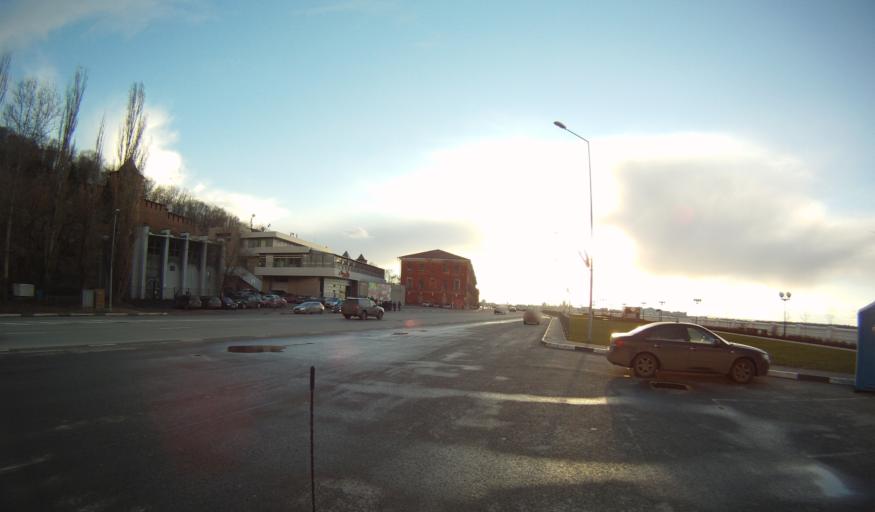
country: RU
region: Nizjnij Novgorod
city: Nizhniy Novgorod
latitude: 56.3320
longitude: 44.0077
